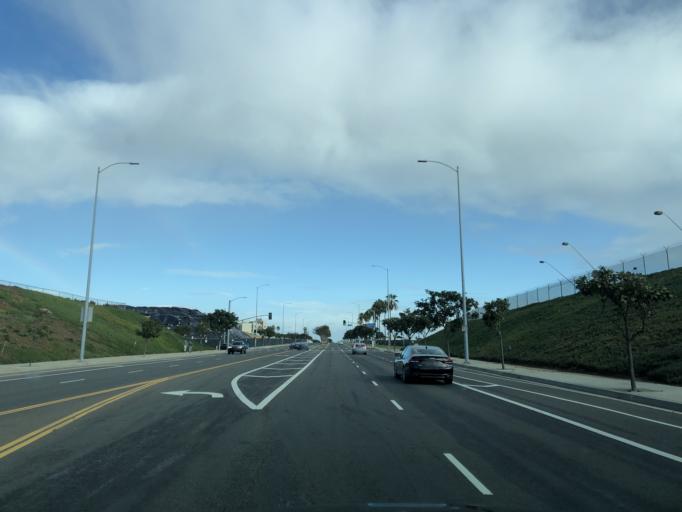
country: US
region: California
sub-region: Los Angeles County
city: El Segundo
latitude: 33.9531
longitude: -118.4187
